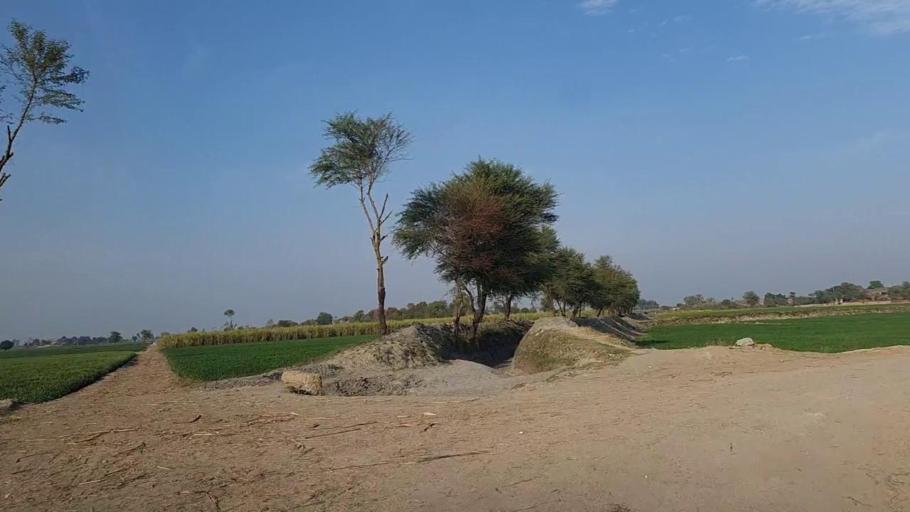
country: PK
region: Sindh
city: Nawabshah
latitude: 26.3704
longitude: 68.4912
